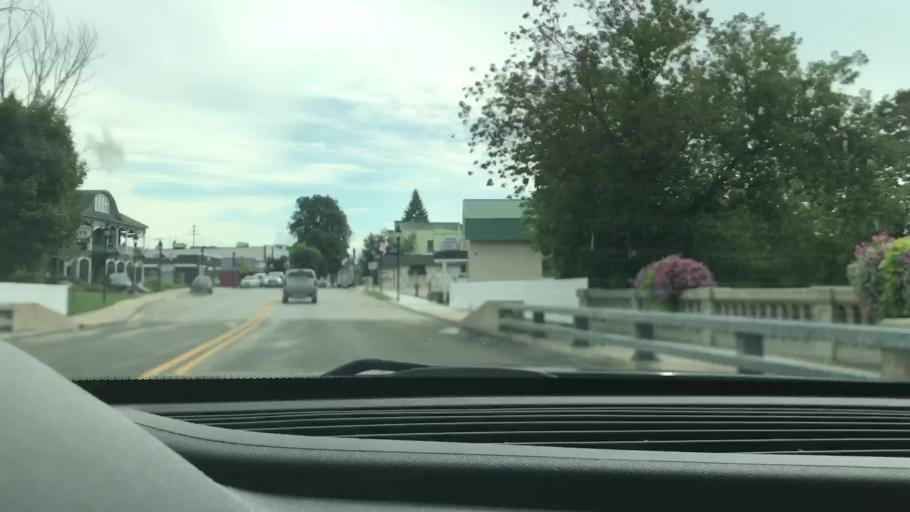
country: US
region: Michigan
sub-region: Antrim County
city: Bellaire
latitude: 44.9787
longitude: -85.2102
